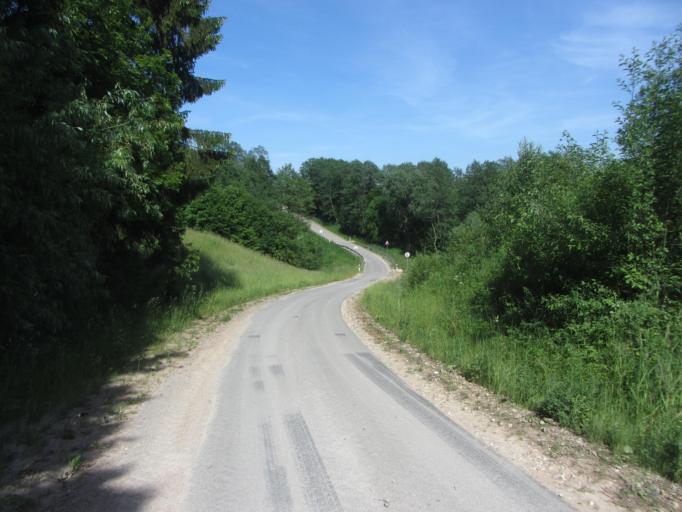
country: LT
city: Jieznas
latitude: 54.5242
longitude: 24.1190
